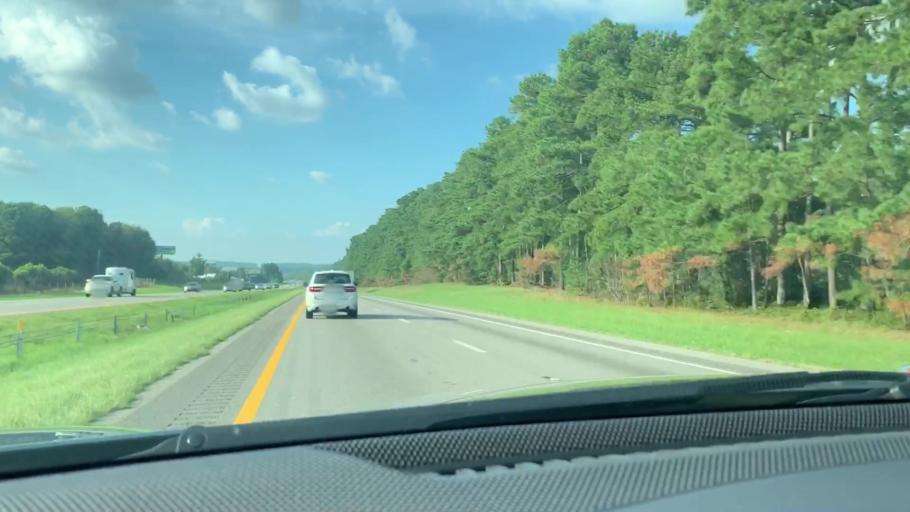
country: US
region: South Carolina
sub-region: Calhoun County
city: Oak Grove
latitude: 33.7029
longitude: -80.9165
